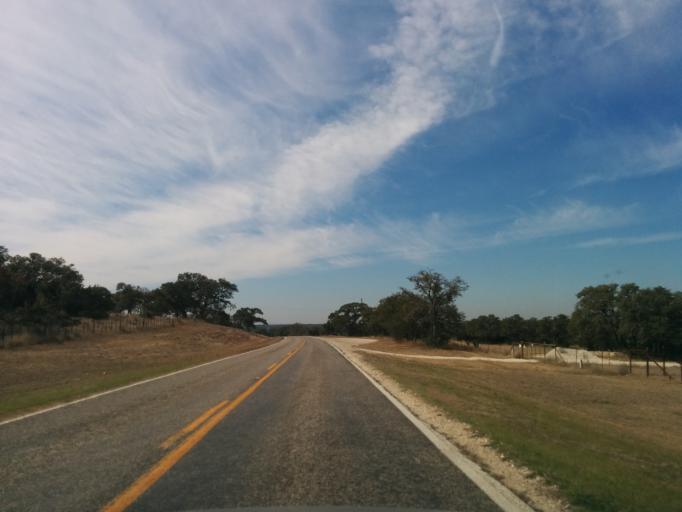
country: US
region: Texas
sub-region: Blanco County
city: Blanco
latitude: 29.9666
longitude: -98.5295
